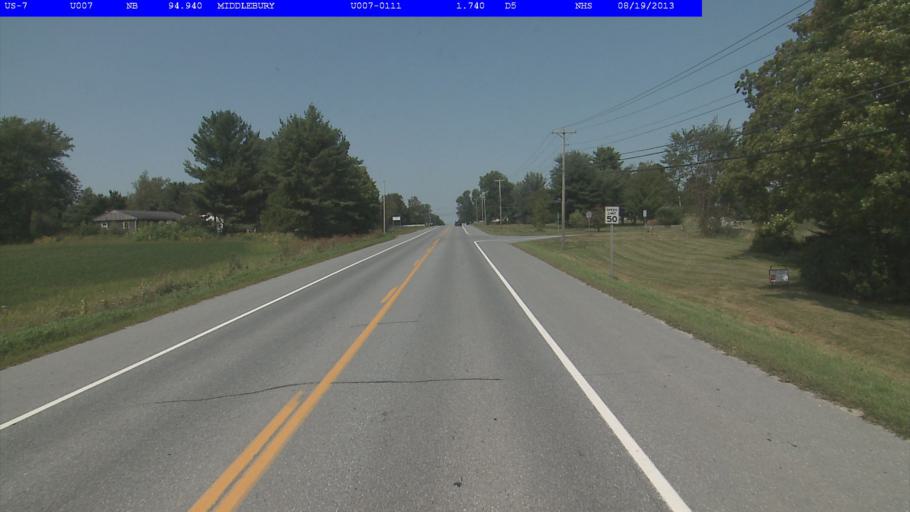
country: US
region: Vermont
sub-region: Addison County
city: Middlebury (village)
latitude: 43.9794
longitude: -73.1227
